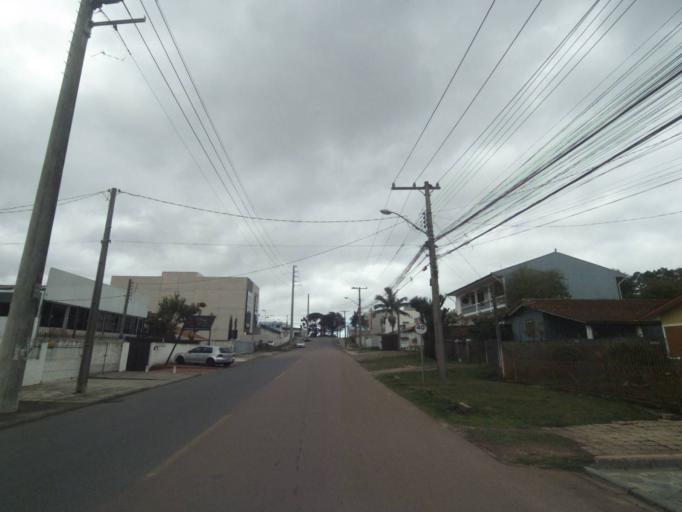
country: BR
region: Parana
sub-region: Sao Jose Dos Pinhais
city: Sao Jose dos Pinhais
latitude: -25.5424
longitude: -49.2959
